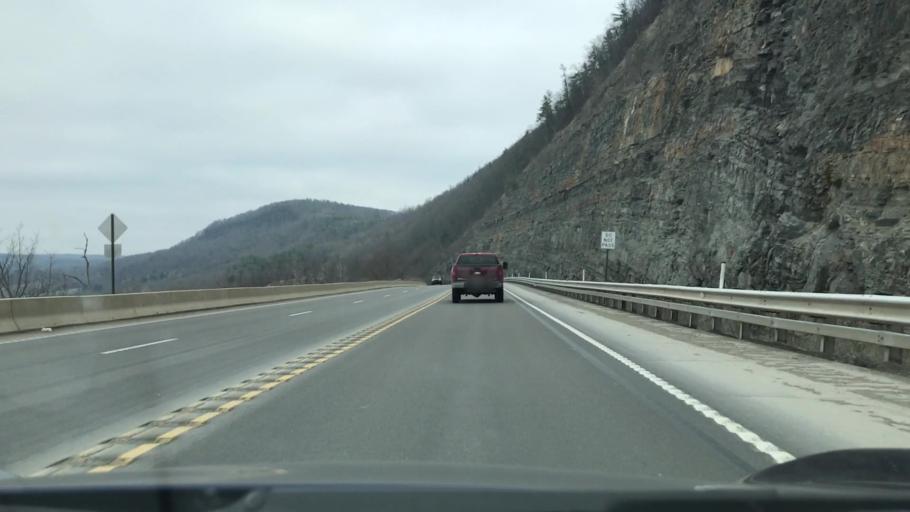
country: US
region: Pennsylvania
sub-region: Bradford County
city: Towanda
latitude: 41.7644
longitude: -76.3695
